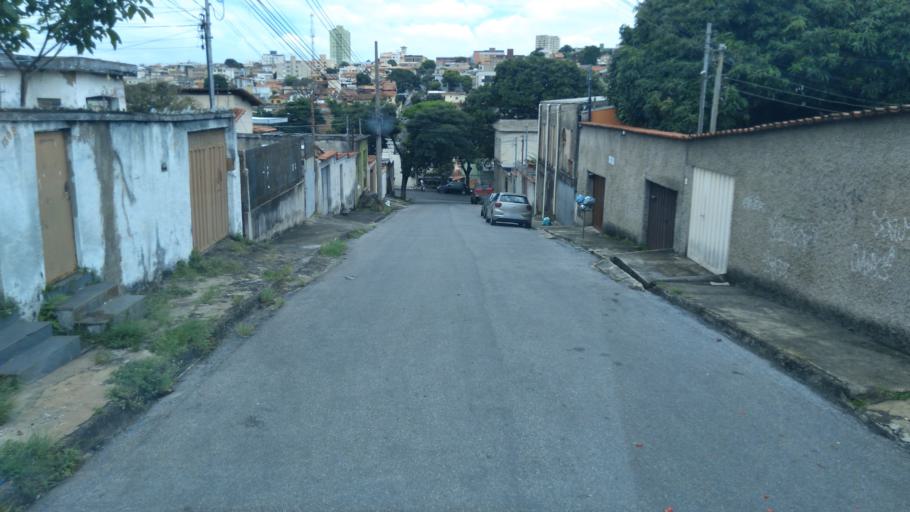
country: BR
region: Minas Gerais
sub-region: Belo Horizonte
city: Belo Horizonte
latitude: -19.9096
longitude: -43.8975
